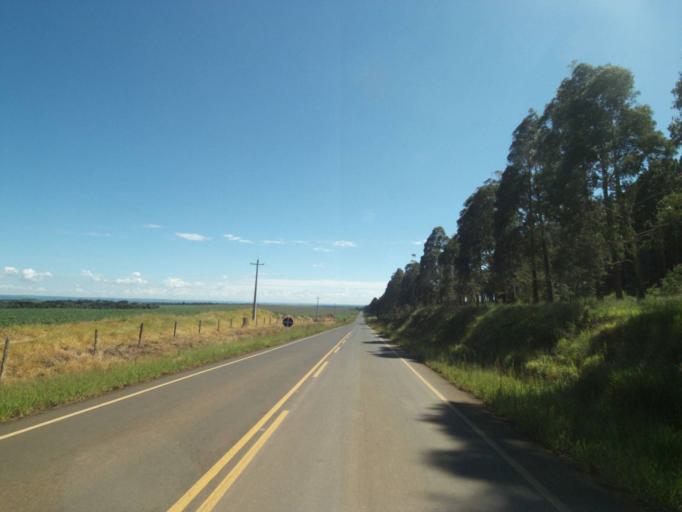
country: BR
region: Parana
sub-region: Pinhao
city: Pinhao
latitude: -25.8321
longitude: -52.0208
